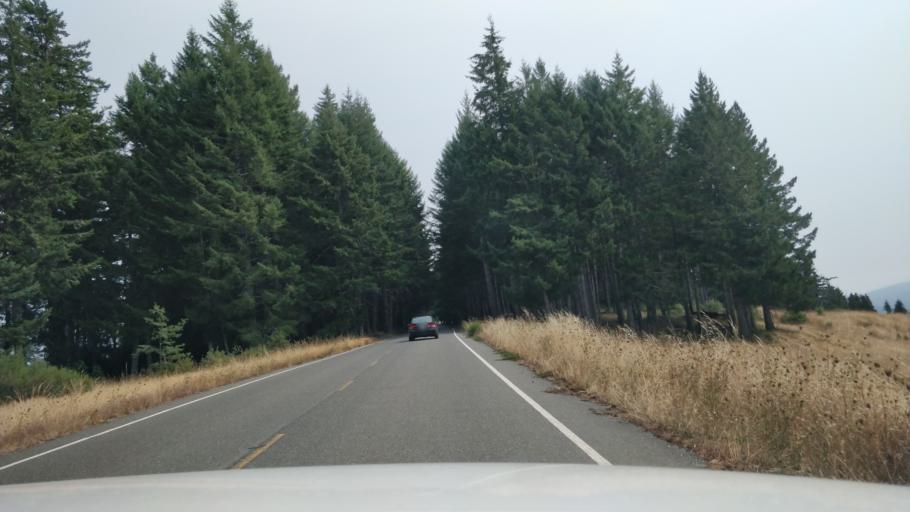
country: US
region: California
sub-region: Humboldt County
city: Westhaven-Moonstone
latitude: 41.2070
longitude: -123.9525
